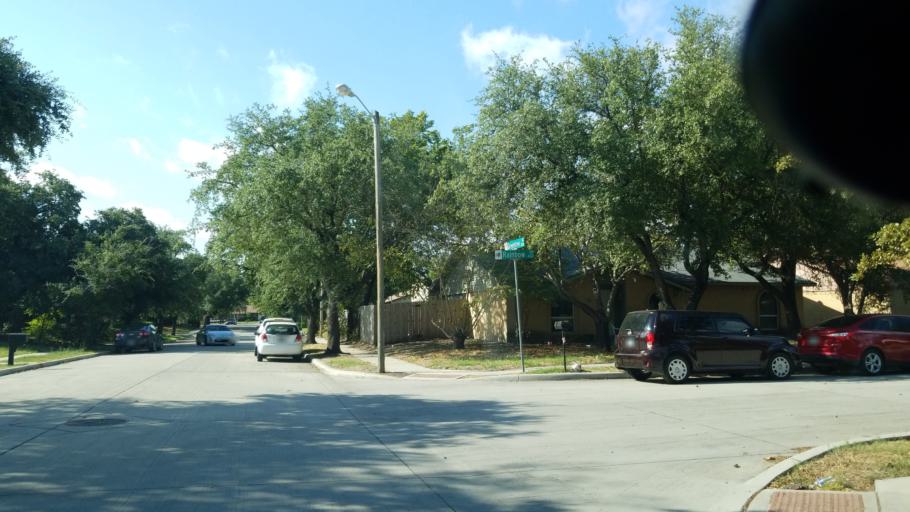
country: US
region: Texas
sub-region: Dallas County
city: Grand Prairie
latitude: 32.6959
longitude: -96.9969
